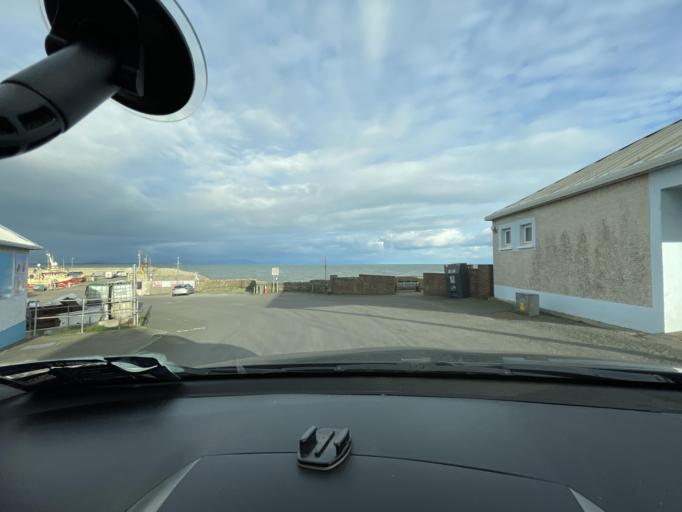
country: IE
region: Leinster
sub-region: Lu
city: Clogherhead
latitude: 53.7976
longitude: -6.2211
